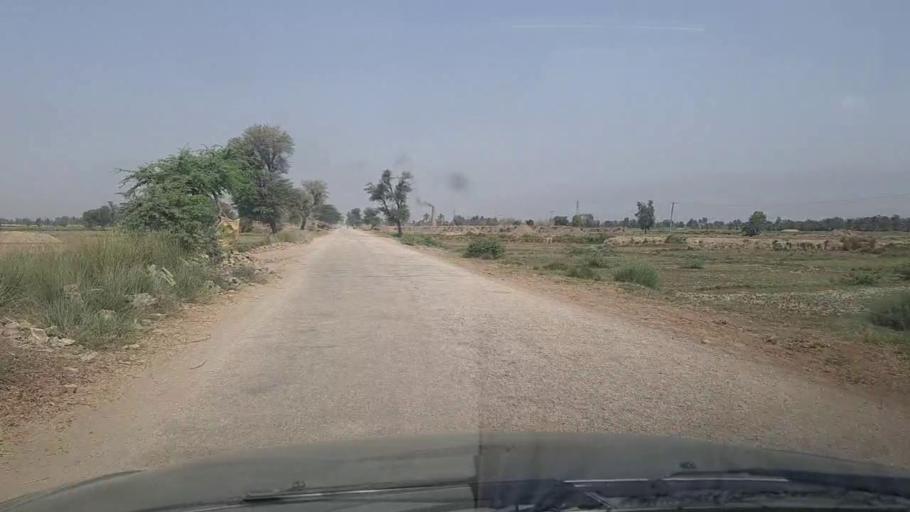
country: PK
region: Sindh
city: Setharja Old
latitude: 27.1456
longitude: 68.5255
